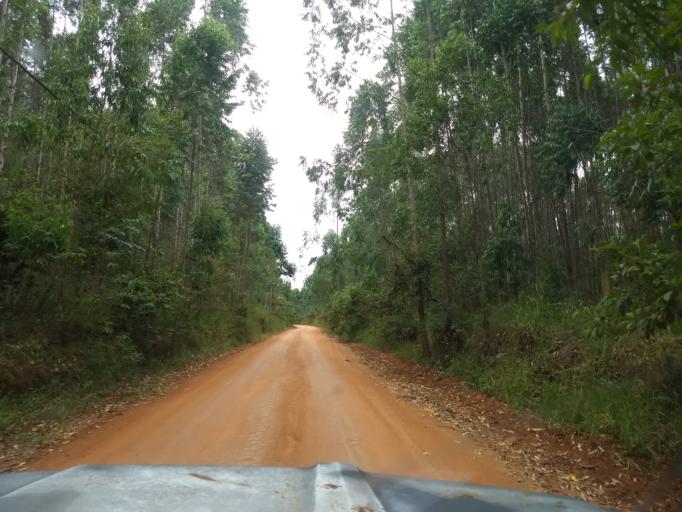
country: BR
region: Sao Paulo
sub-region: Cabreuva
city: Cabreuva
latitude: -23.3884
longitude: -47.1953
